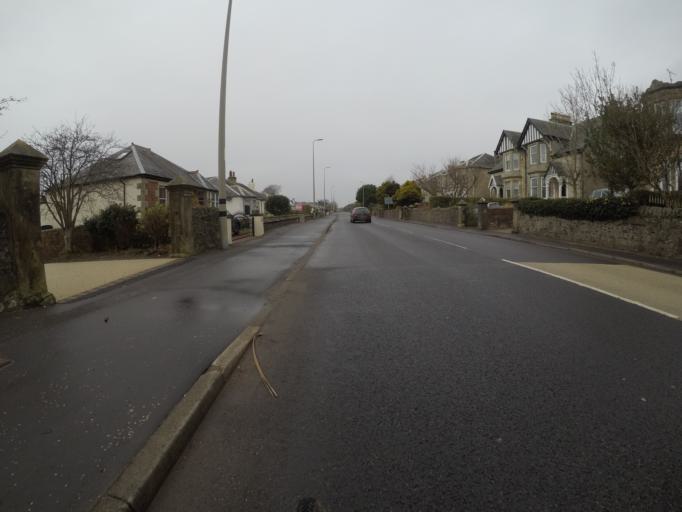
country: GB
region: Scotland
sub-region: North Ayrshire
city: West Kilbride
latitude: 55.6901
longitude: -4.8647
